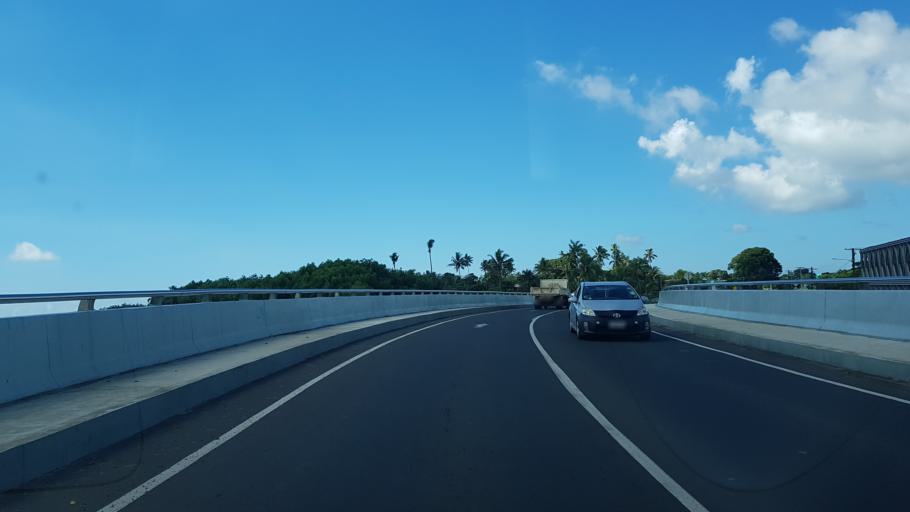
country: FJ
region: Central
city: Suva
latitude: -18.1382
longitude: 178.4585
